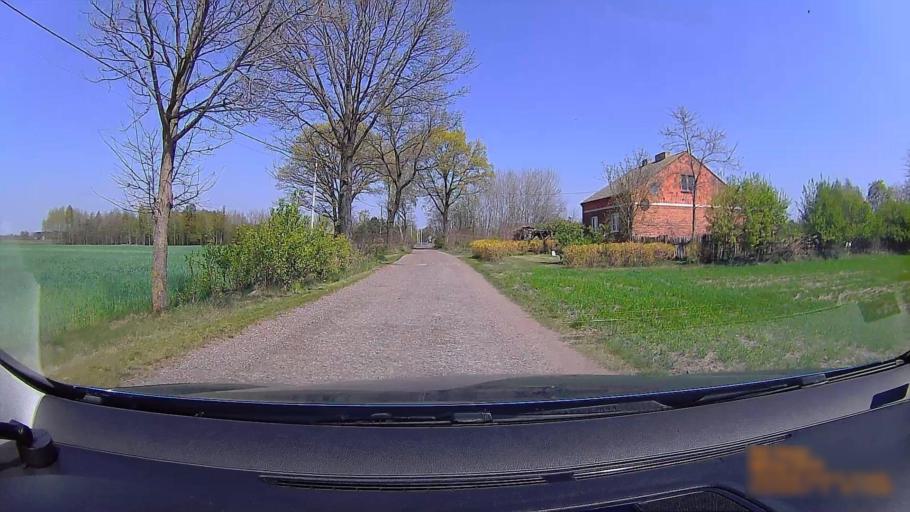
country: PL
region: Greater Poland Voivodeship
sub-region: Powiat koninski
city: Rychwal
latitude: 52.0945
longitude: 18.1834
